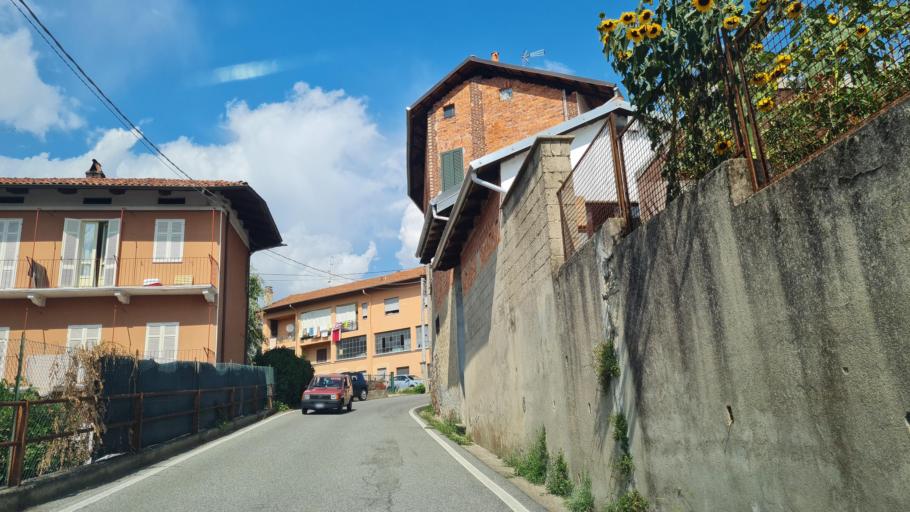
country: IT
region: Piedmont
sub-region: Provincia di Biella
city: Cossato
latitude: 45.5799
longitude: 8.1823
